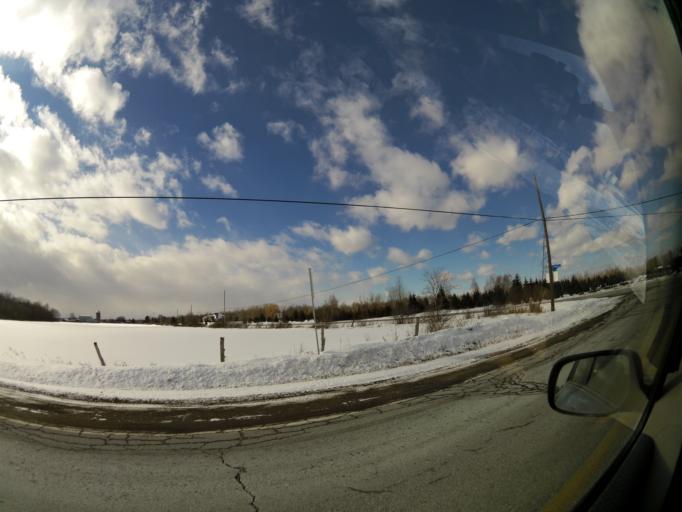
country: CA
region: Ontario
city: Ottawa
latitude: 45.3252
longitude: -75.5149
